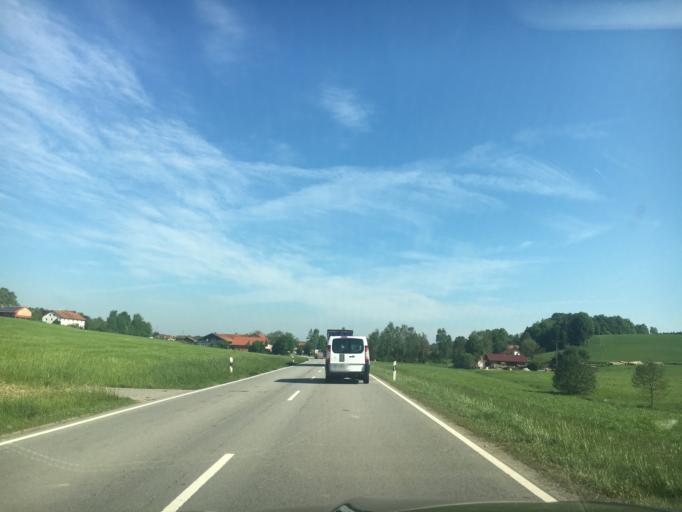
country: DE
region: Bavaria
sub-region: Upper Bavaria
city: Rohrbach
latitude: 48.3096
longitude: 12.5614
